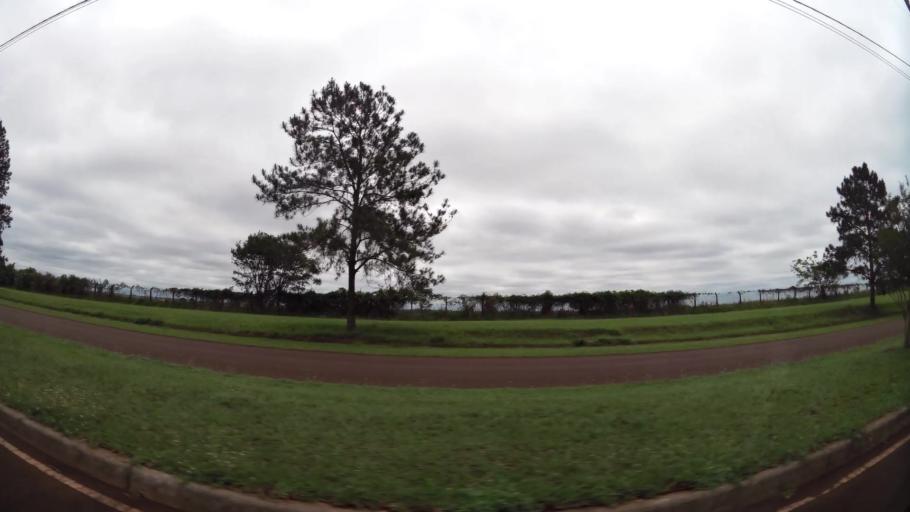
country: PY
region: Alto Parana
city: Colonia Yguazu
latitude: -25.4720
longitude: -54.8551
